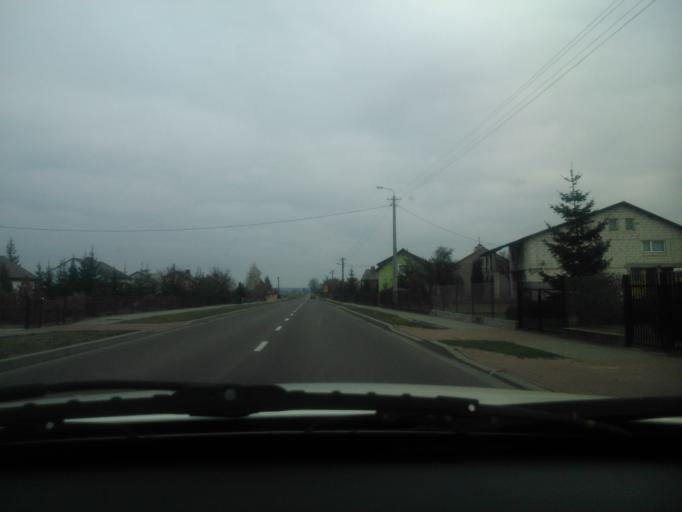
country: PL
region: Masovian Voivodeship
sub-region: Powiat mlawski
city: Lipowiec Koscielny
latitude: 53.1060
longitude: 20.1873
